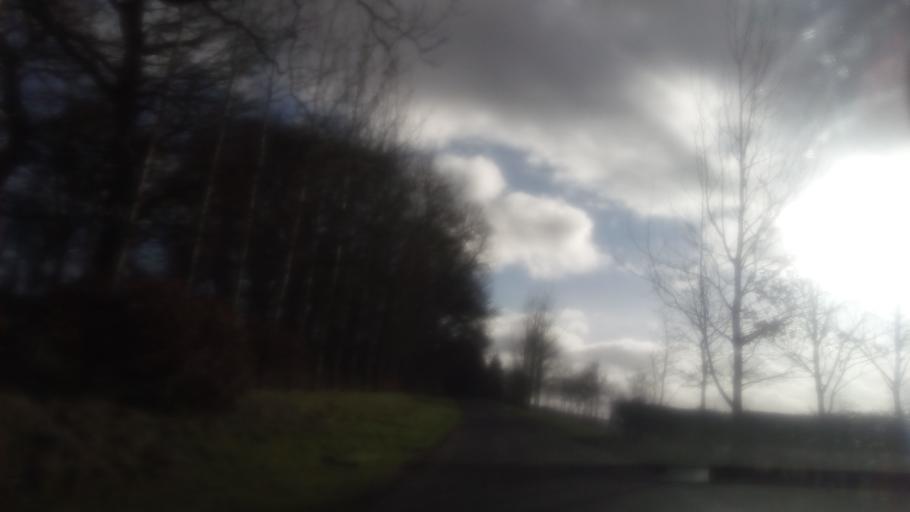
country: GB
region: Scotland
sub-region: The Scottish Borders
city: Jedburgh
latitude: 55.4754
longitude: -2.6144
